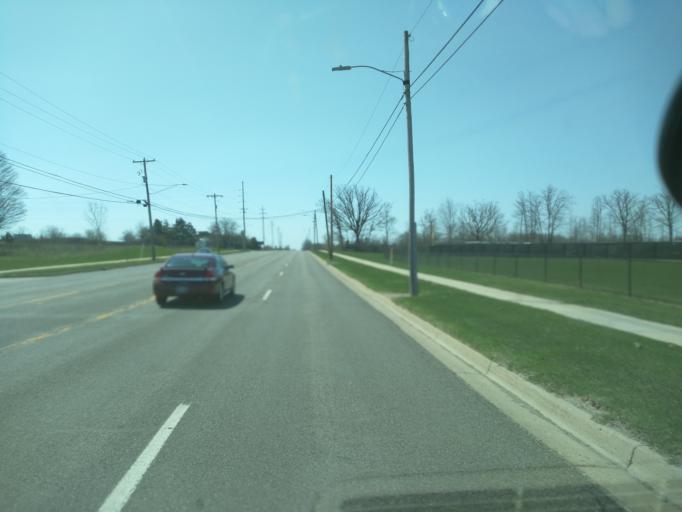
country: US
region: Michigan
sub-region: Kent County
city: East Grand Rapids
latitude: 42.9322
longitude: -85.5700
